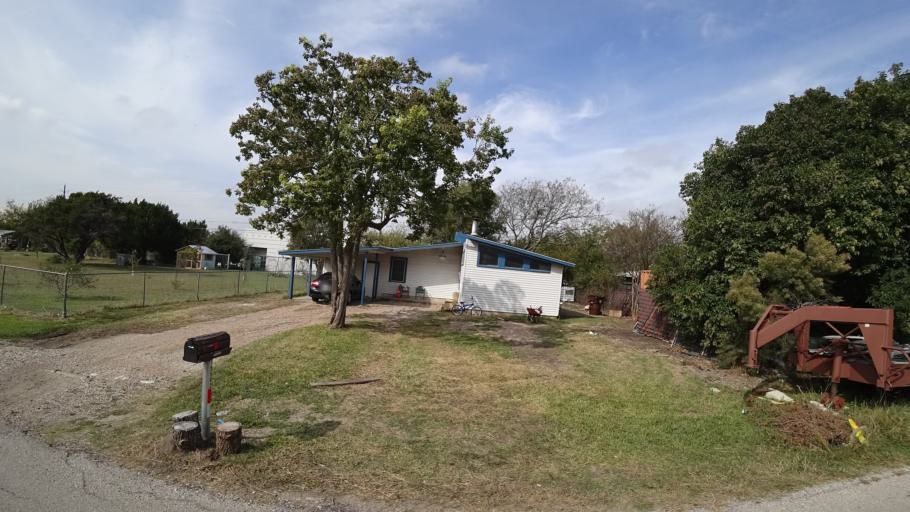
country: US
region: Texas
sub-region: Travis County
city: Wells Branch
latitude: 30.4528
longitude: -97.6711
